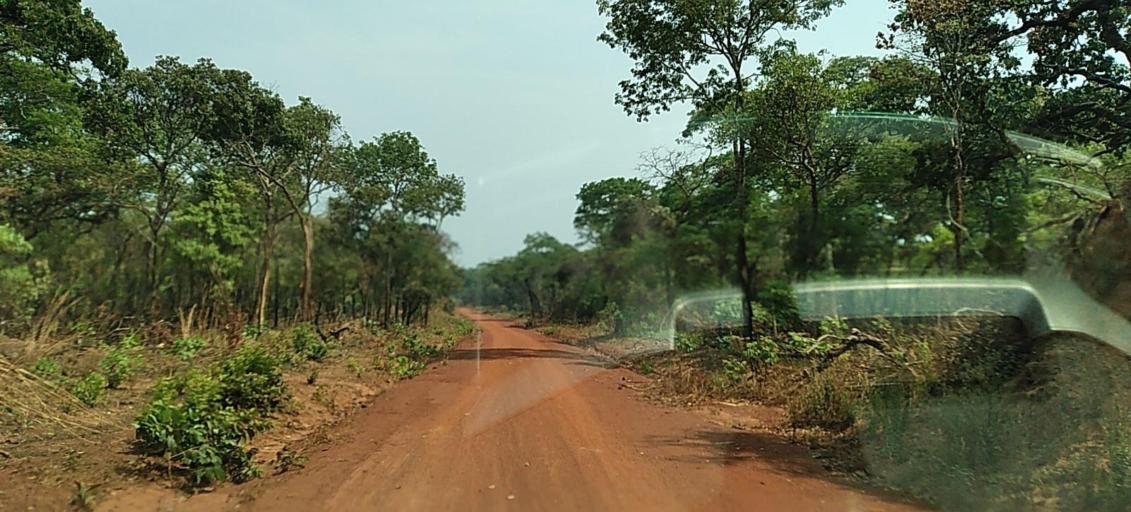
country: ZM
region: North-Western
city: Kansanshi
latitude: -12.0048
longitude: 26.8431
